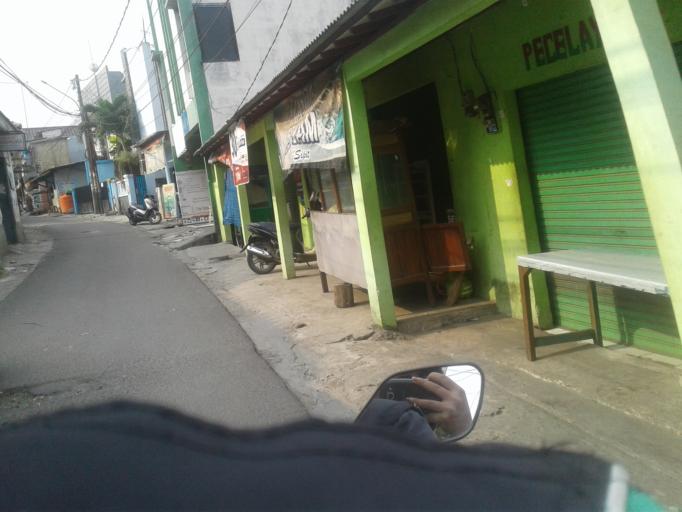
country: ID
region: West Java
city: Depok
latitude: -6.3677
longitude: 106.8370
